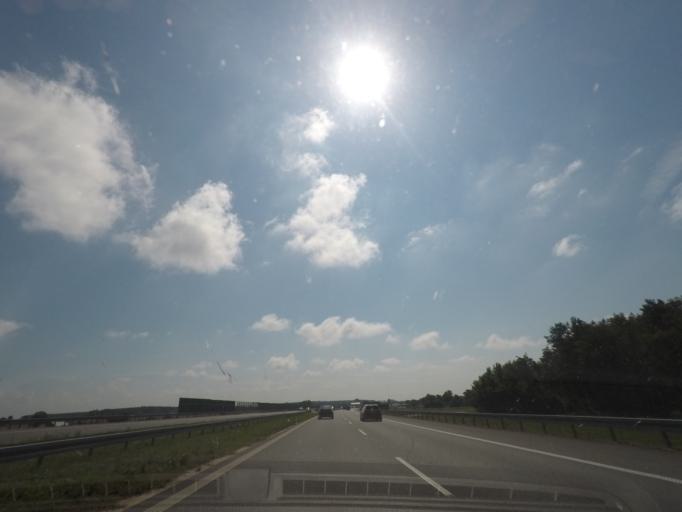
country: PL
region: Kujawsko-Pomorskie
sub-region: Powiat wloclawski
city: Baruchowo
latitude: 52.4554
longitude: 19.2146
